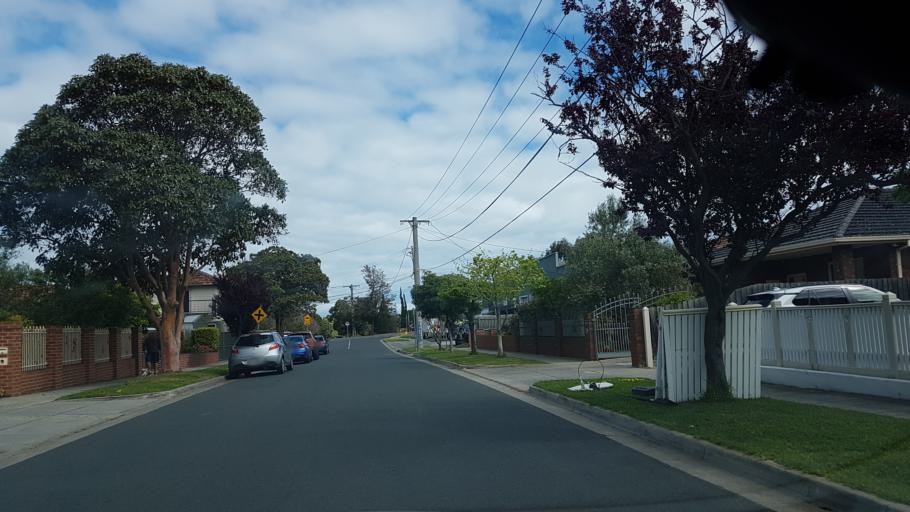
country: AU
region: Victoria
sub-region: Glen Eira
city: Bentleigh
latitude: -37.9213
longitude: 145.0368
